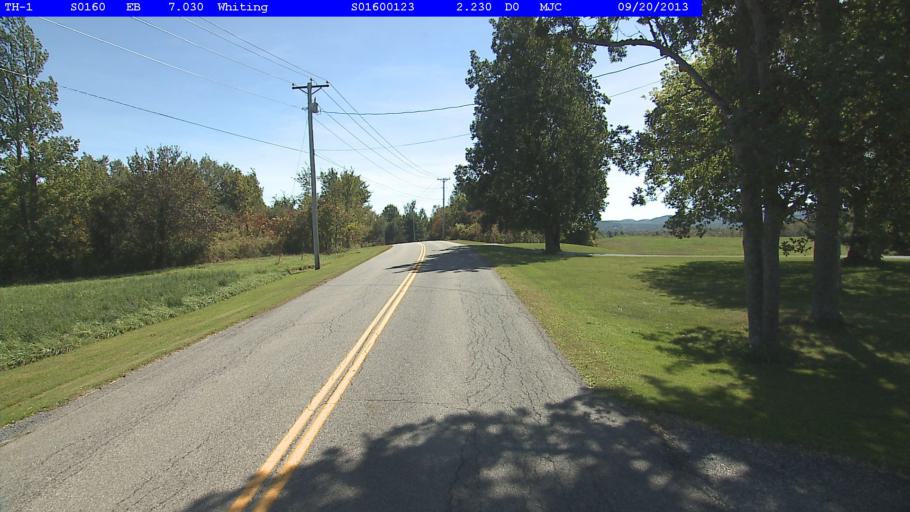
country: US
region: Vermont
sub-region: Rutland County
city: Brandon
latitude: 43.8568
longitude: -73.1845
